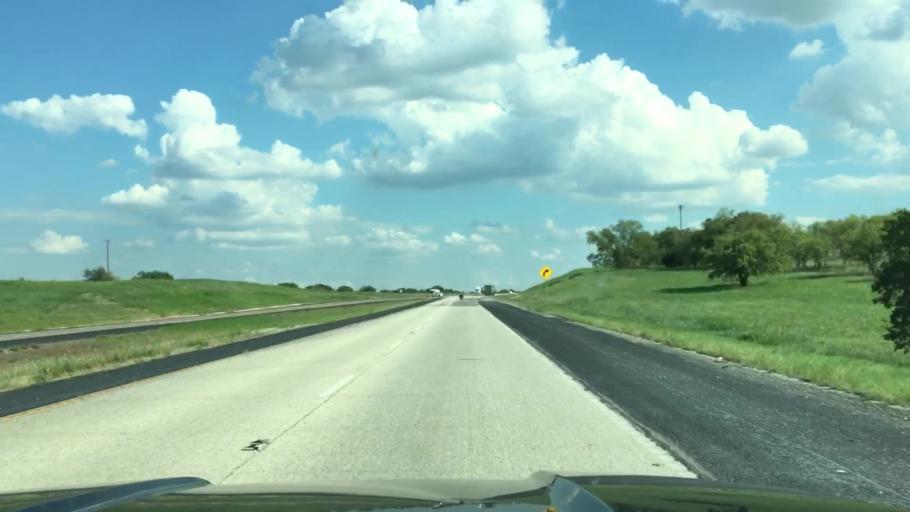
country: US
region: Texas
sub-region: Wise County
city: New Fairview
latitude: 33.1222
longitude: -97.4862
